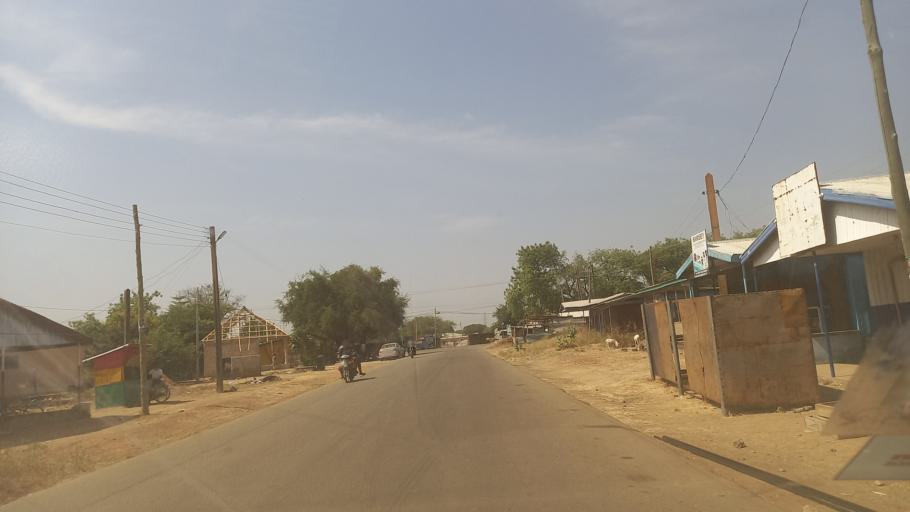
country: GH
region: Upper East
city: Navrongo
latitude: 10.8822
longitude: -1.0834
